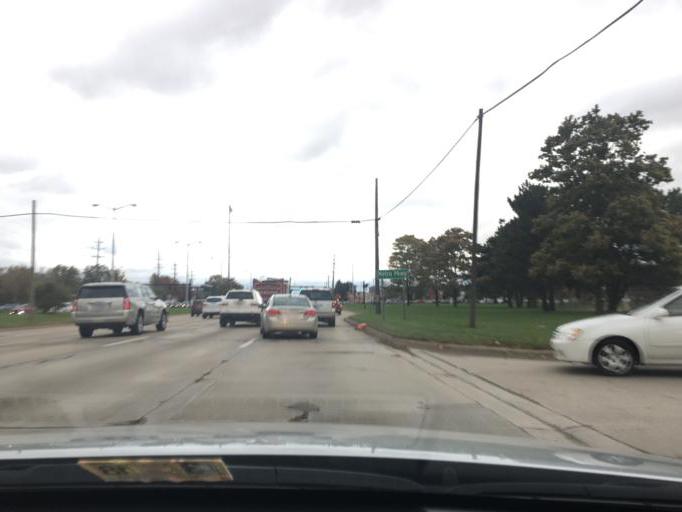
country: US
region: Michigan
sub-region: Macomb County
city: Sterling Heights
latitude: 42.5634
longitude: -83.0488
